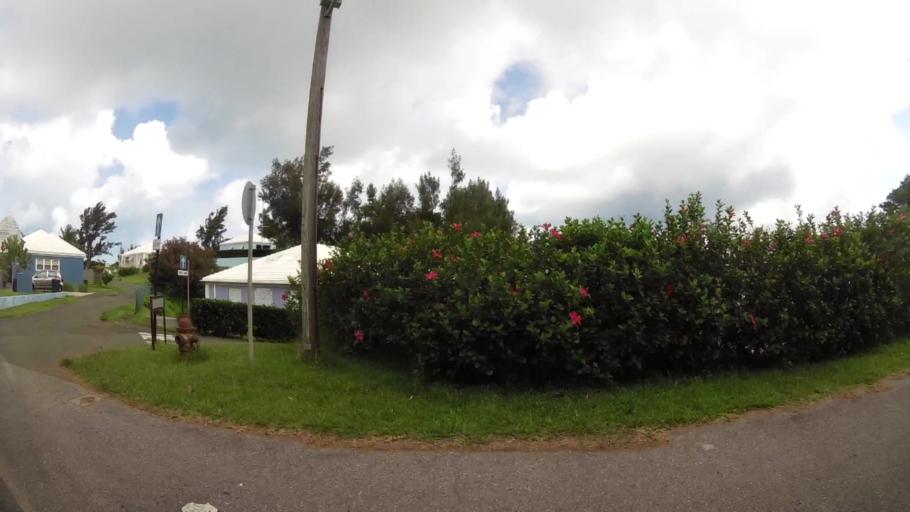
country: BM
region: Saint George
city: Saint George
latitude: 32.3684
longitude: -64.6745
